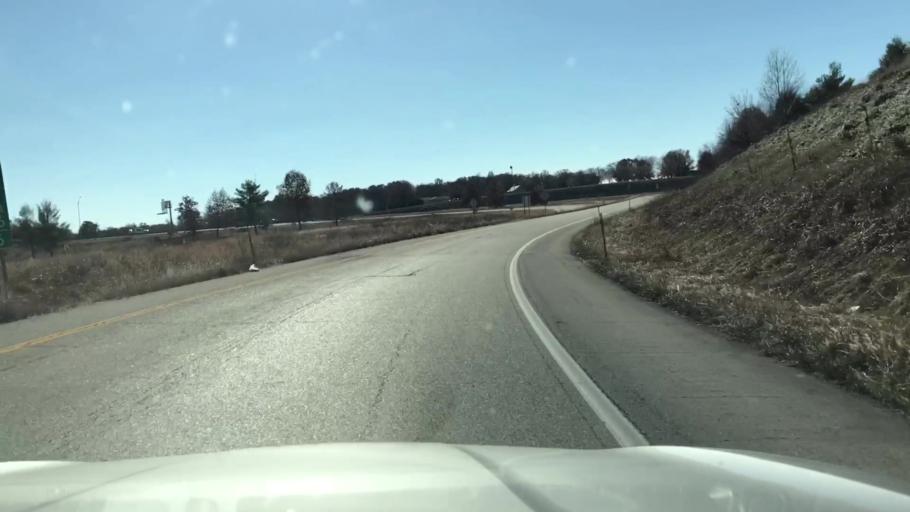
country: US
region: Missouri
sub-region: Jasper County
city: Carthage
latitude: 37.0843
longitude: -94.3129
